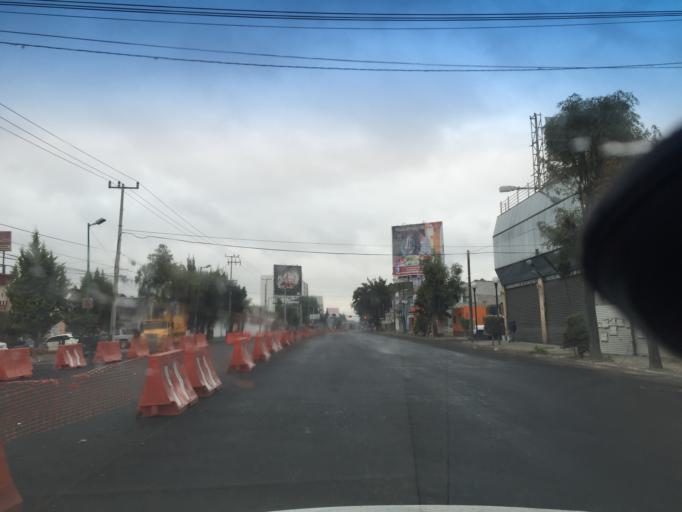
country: MX
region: Mexico
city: Colonia Lindavista
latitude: 19.4922
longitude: -99.1404
